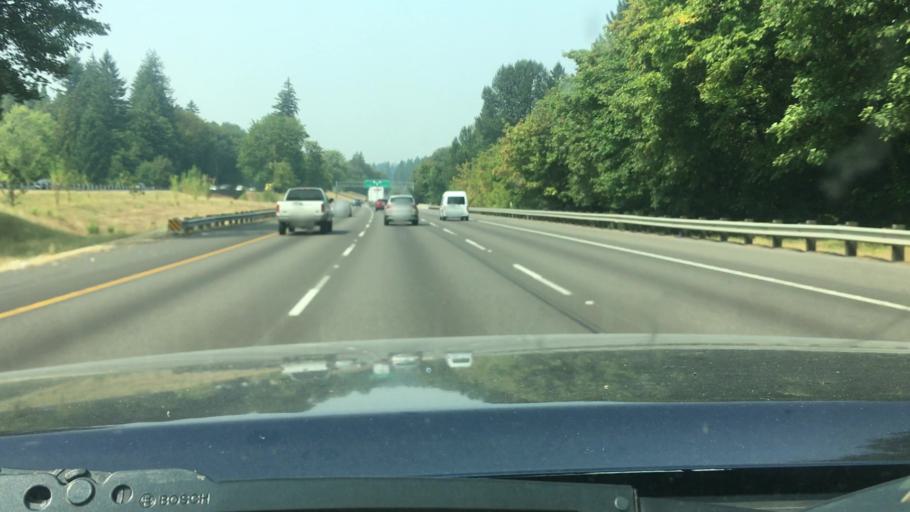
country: US
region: Oregon
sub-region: Clackamas County
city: Stafford
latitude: 45.3735
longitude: -122.7245
